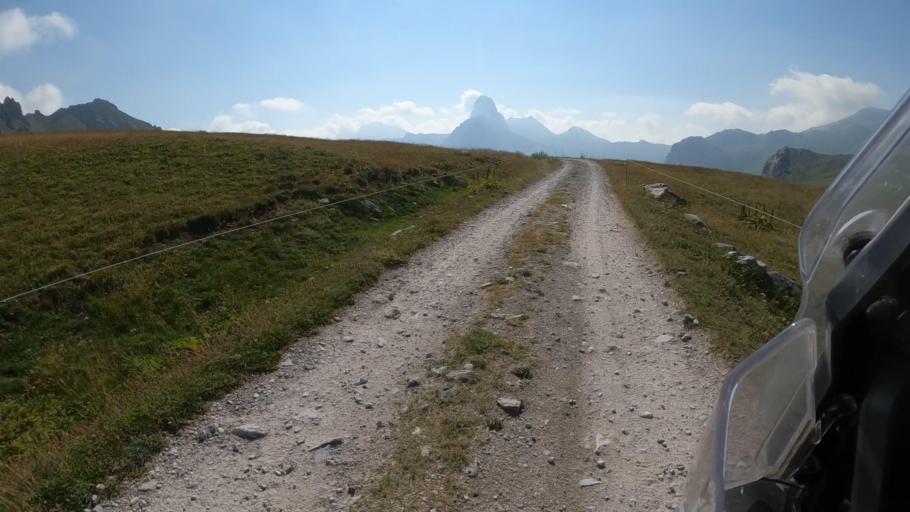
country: IT
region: Piedmont
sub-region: Provincia di Cuneo
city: Bersezio
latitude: 44.4067
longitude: 7.0180
